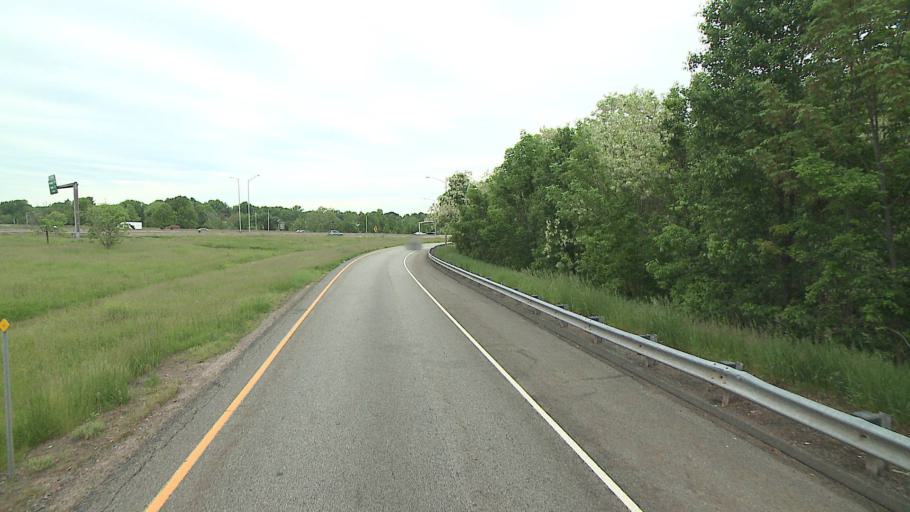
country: US
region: Connecticut
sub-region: Hartford County
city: Windsor
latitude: 41.8762
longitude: -72.6611
